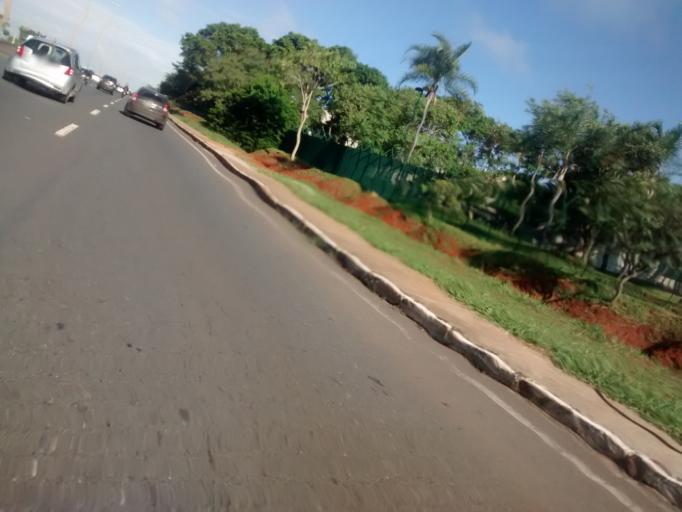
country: BR
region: Federal District
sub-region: Brasilia
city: Brasilia
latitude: -15.8157
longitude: -47.8381
